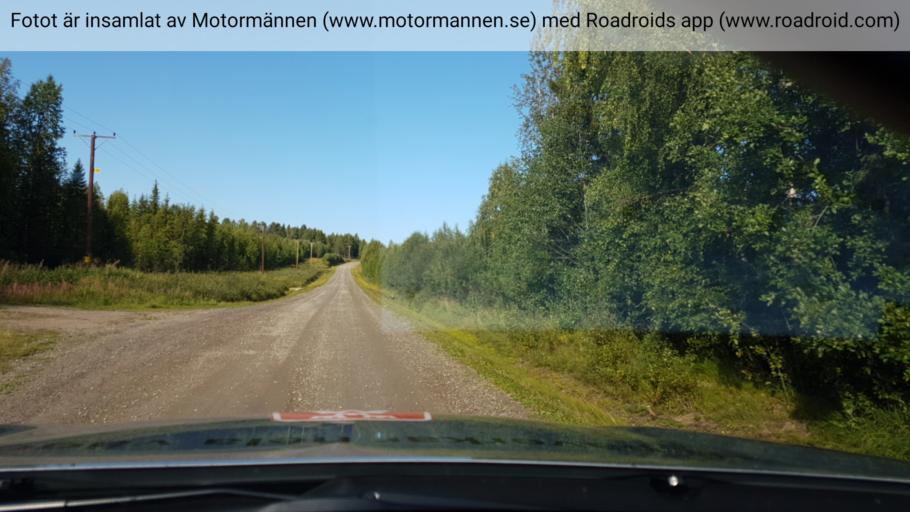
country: SE
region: Norrbotten
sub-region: Kalix Kommun
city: Kalix
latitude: 66.1347
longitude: 23.2417
